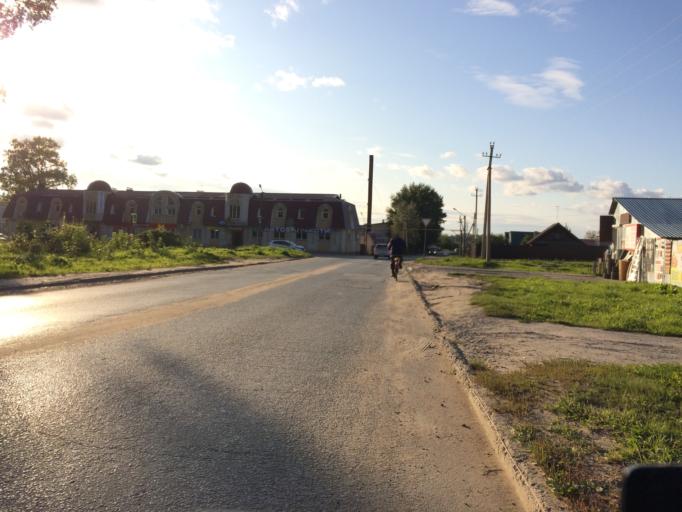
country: RU
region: Mariy-El
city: Yoshkar-Ola
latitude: 56.6505
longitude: 47.9596
